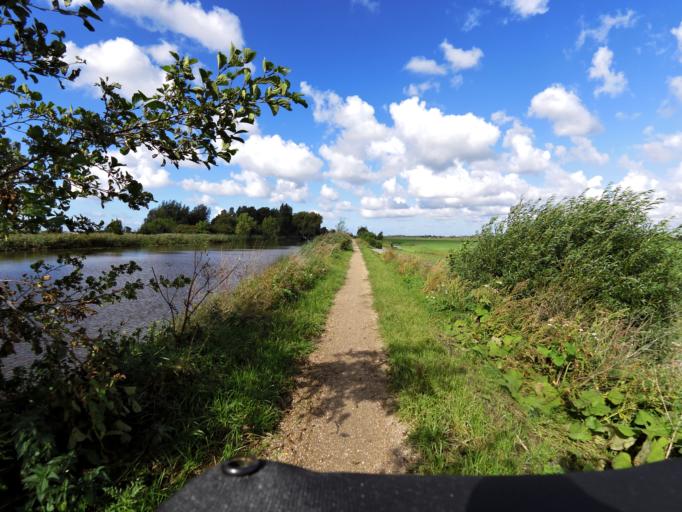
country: NL
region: South Holland
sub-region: Gemeente Vlaardingen
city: Vlaardingen
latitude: 51.9490
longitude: 4.3198
